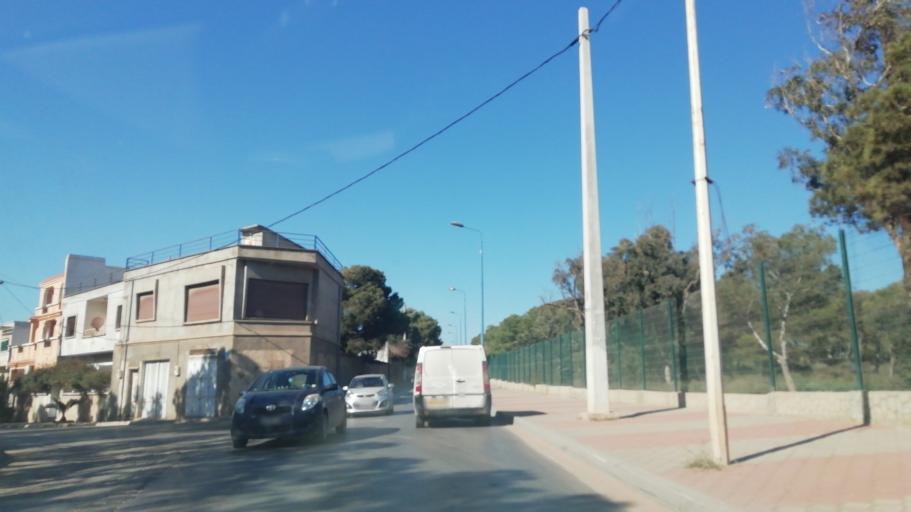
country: DZ
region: Oran
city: Bir el Djir
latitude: 35.7438
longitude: -0.5685
